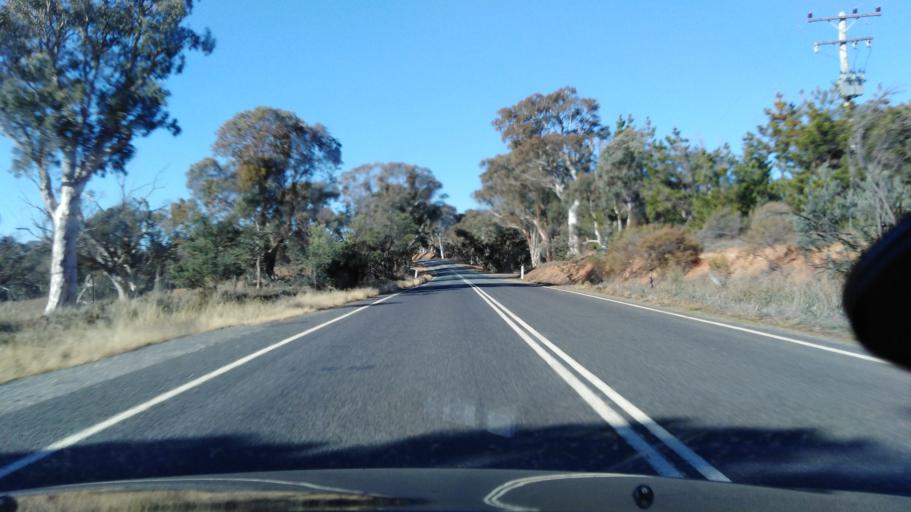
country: AU
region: New South Wales
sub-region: Yass Valley
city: Gundaroo
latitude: -35.1817
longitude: 149.2764
